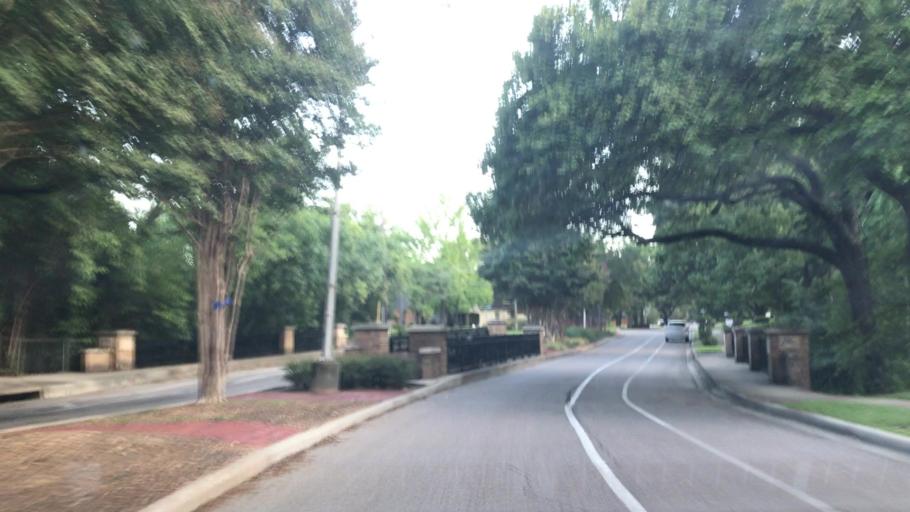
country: US
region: Texas
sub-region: Dallas County
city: Richardson
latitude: 32.9580
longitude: -96.7561
